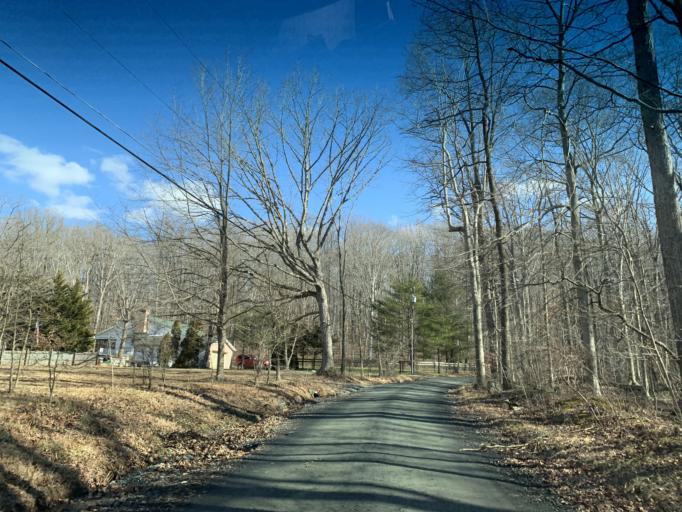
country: US
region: Maryland
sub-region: Harford County
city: Riverside
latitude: 39.5087
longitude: -76.2481
